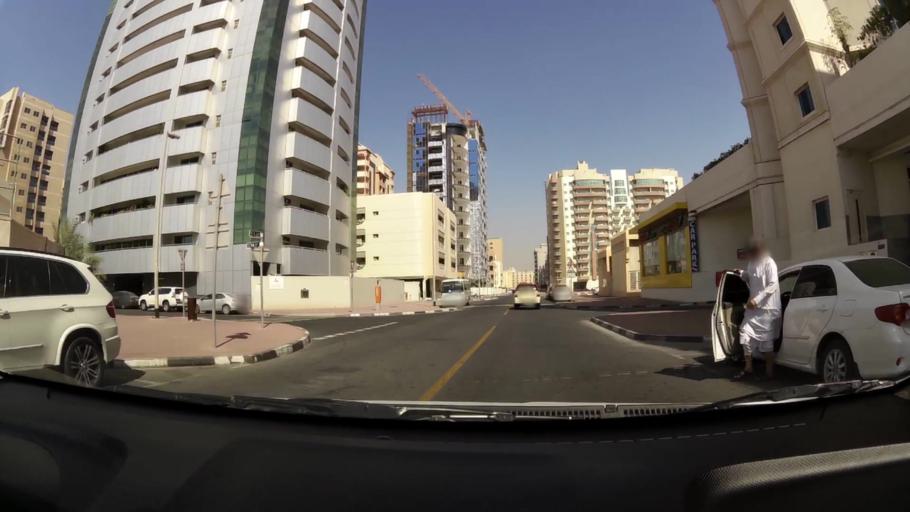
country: AE
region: Ash Shariqah
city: Sharjah
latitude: 25.2757
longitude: 55.3686
